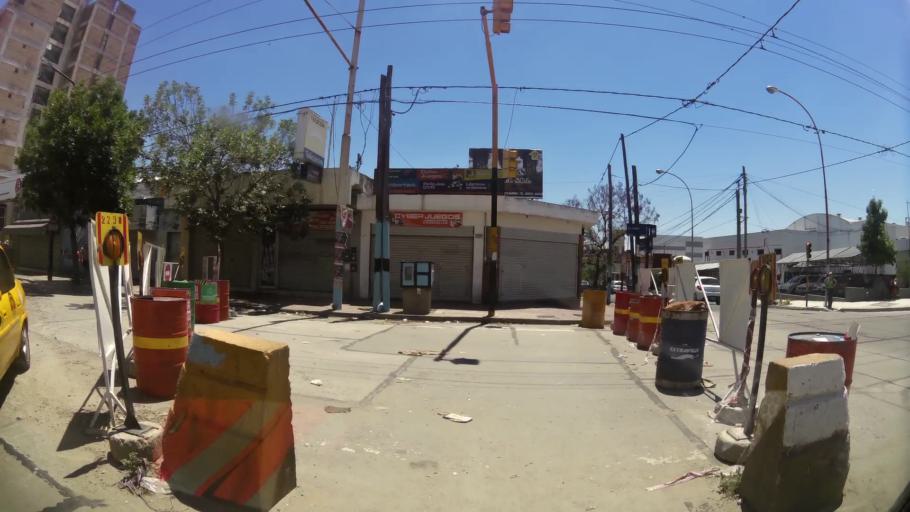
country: AR
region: Cordoba
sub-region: Departamento de Capital
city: Cordoba
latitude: -31.4049
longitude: -64.2127
